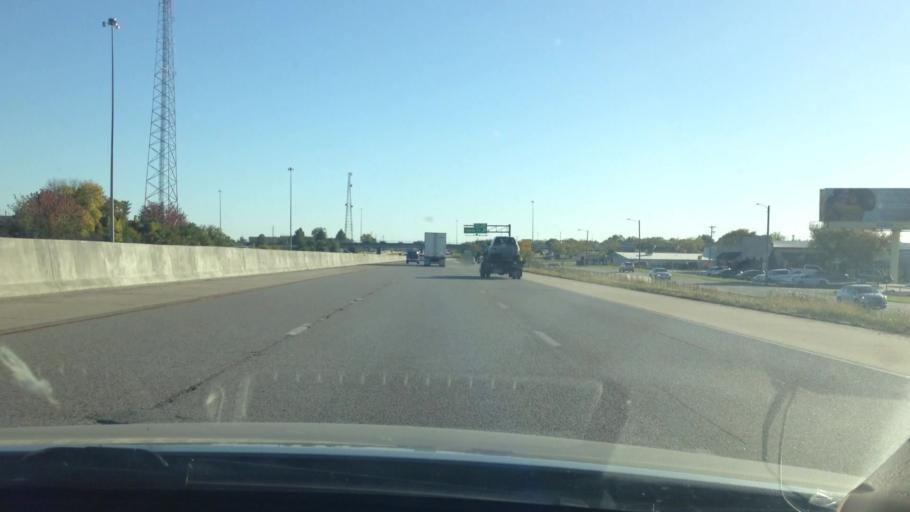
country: US
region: Kansas
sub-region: Johnson County
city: Olathe
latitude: 38.8890
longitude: -94.7898
